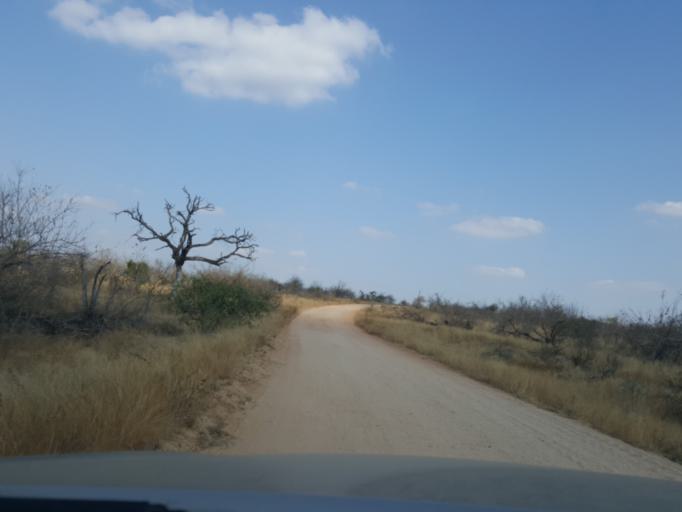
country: ZA
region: Mpumalanga
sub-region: Ehlanzeni District
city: Komatipoort
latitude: -25.2982
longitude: 31.7580
